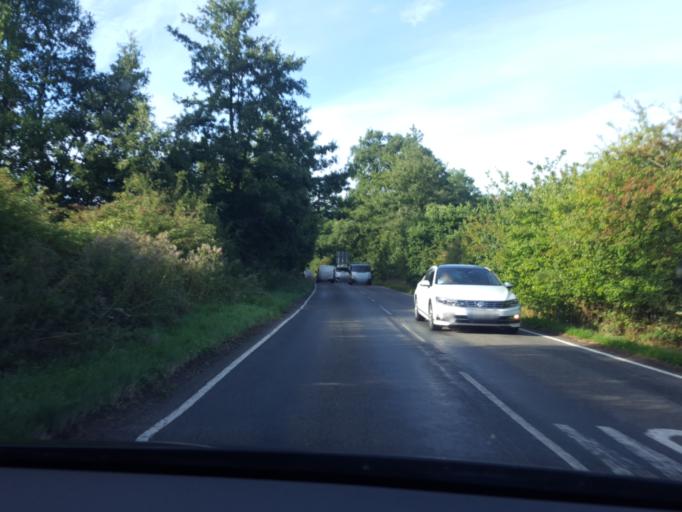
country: GB
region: England
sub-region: Leicestershire
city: Shepshed
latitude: 52.7321
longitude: -1.2727
